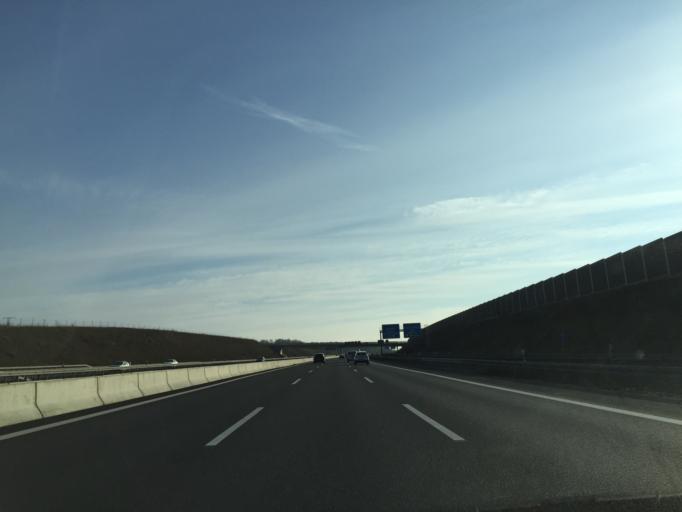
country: DE
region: Bavaria
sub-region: Regierungsbezirk Unterfranken
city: Eisingen
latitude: 49.7492
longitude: 9.8313
